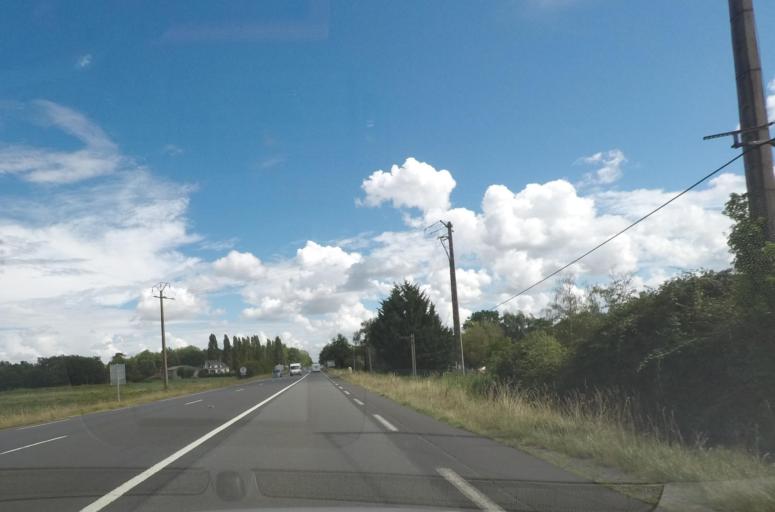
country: FR
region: Pays de la Loire
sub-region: Departement de la Sarthe
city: Parigne-le-Polin
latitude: 47.8558
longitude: 0.1012
